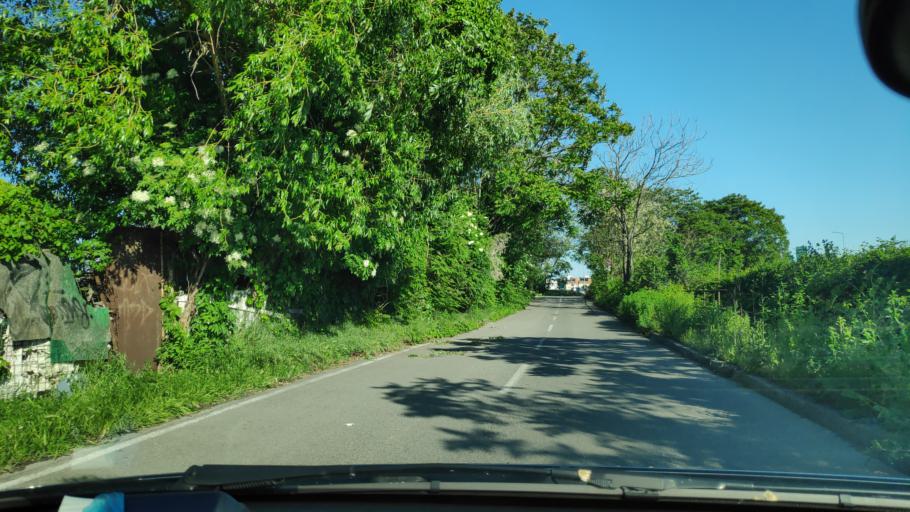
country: IT
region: Lombardy
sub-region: Citta metropolitana di Milano
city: Linate
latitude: 45.4444
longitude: 9.2560
